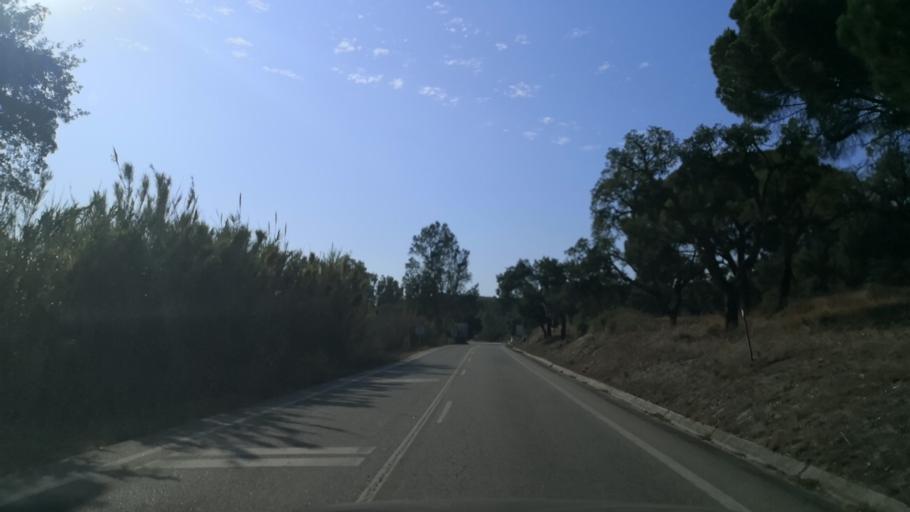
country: PT
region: Santarem
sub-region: Almeirim
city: Fazendas de Almeirim
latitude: 39.1143
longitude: -8.5783
